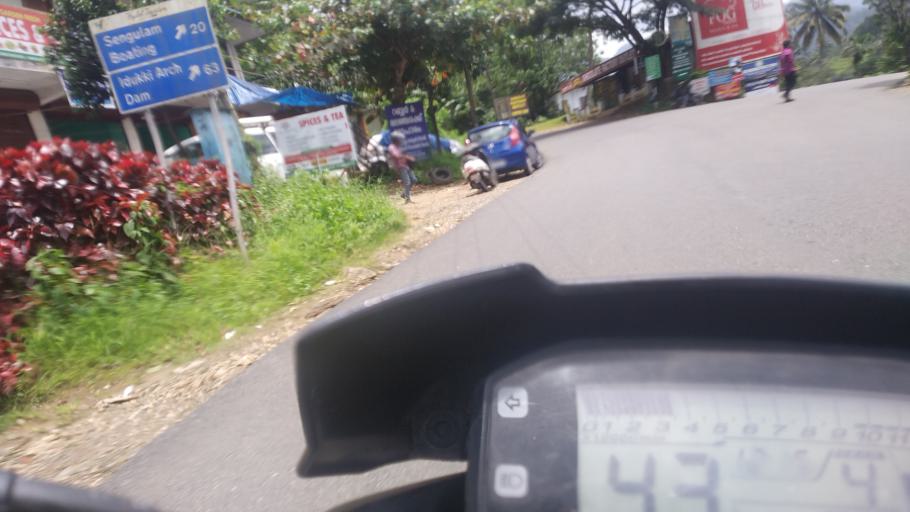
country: IN
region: Kerala
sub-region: Idukki
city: Munnar
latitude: 10.0131
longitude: 77.0100
